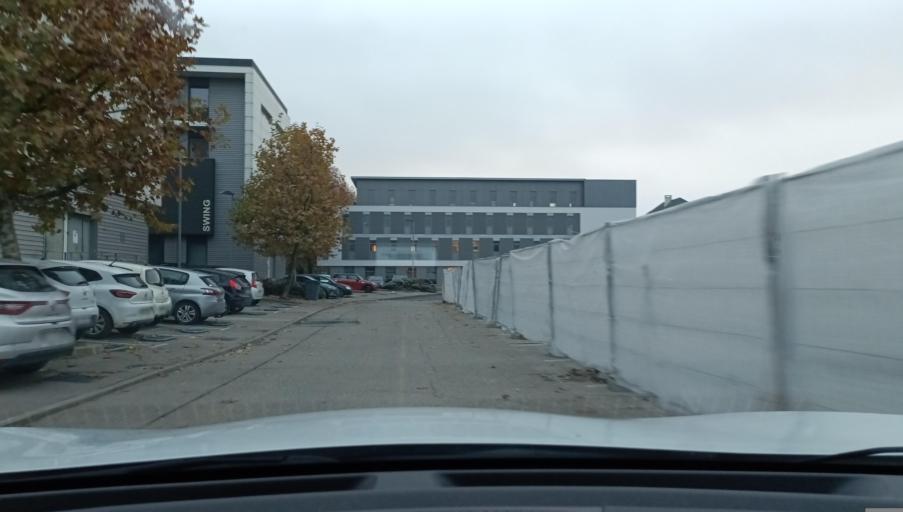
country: FR
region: Rhone-Alpes
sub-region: Departement de l'Isere
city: Vienne
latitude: 45.5150
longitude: 4.8649
